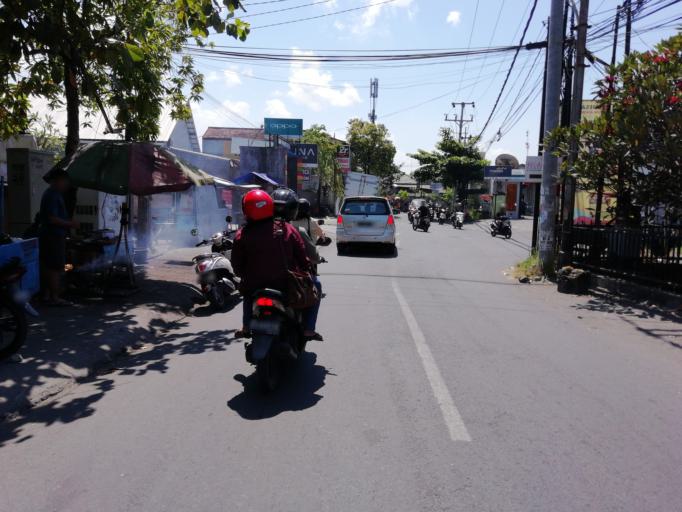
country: ID
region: Bali
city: Karyadharma
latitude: -8.6942
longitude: 115.1920
